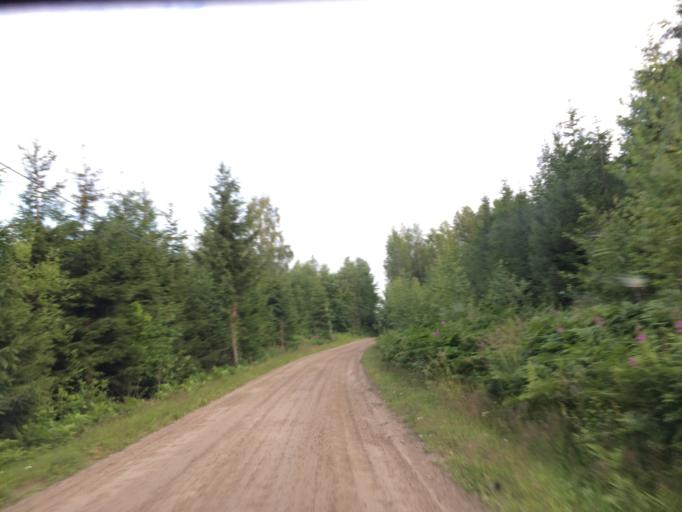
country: FI
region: Haeme
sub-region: Haemeenlinna
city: Janakkala
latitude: 60.8855
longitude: 24.6104
